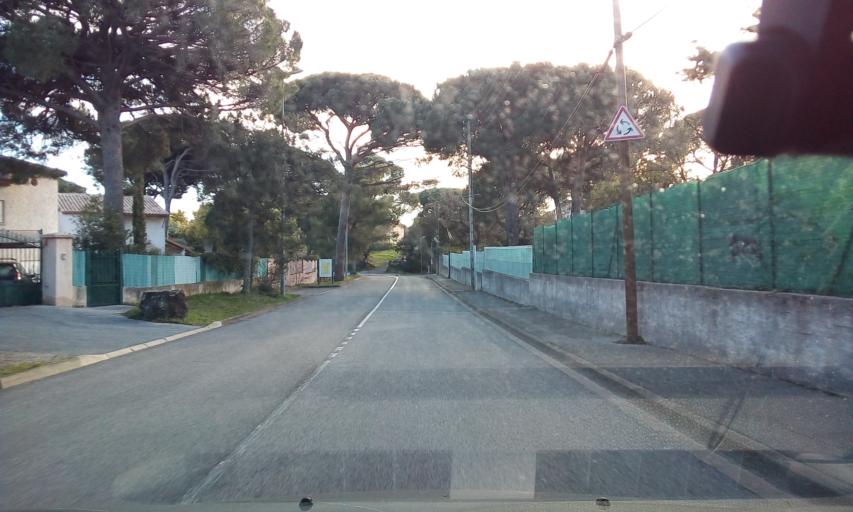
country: FR
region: Provence-Alpes-Cote d'Azur
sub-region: Departement du Var
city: Saint-Raphael
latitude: 43.4420
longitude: 6.7674
